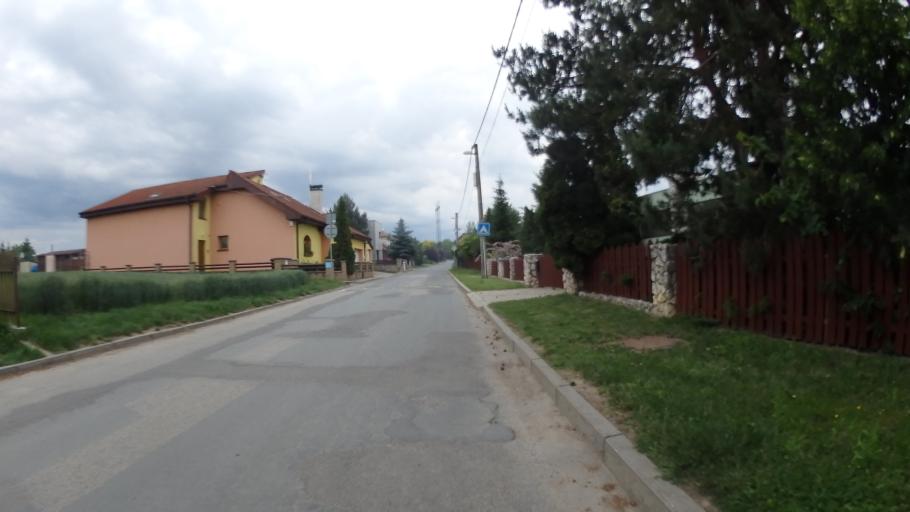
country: CZ
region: South Moravian
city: Ostopovice
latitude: 49.1398
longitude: 16.5537
